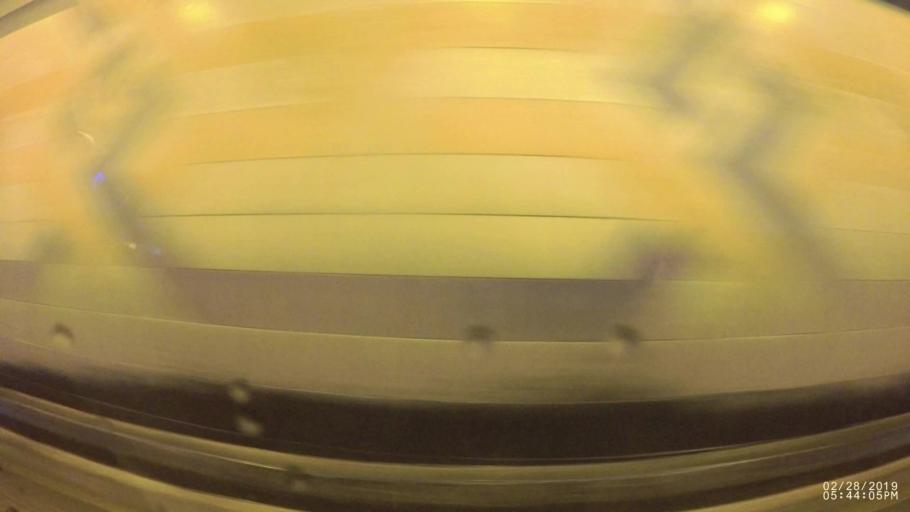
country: JO
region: Amman
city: Al Jubayhah
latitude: 31.9914
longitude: 35.8686
